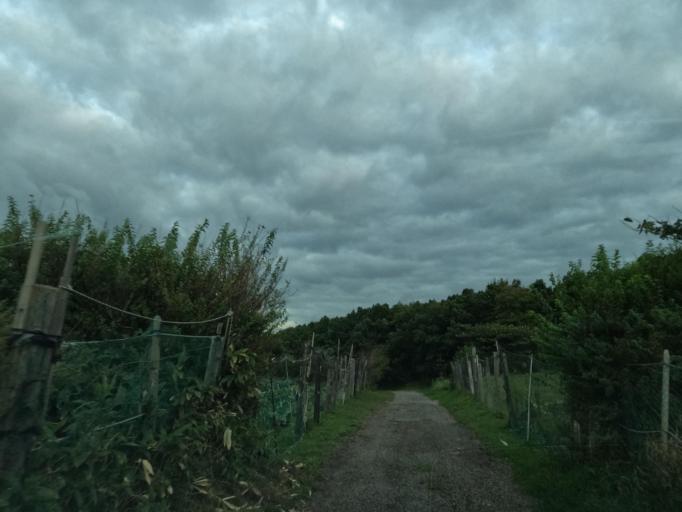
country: JP
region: Hokkaido
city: Muroran
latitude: 42.3708
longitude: 140.9712
